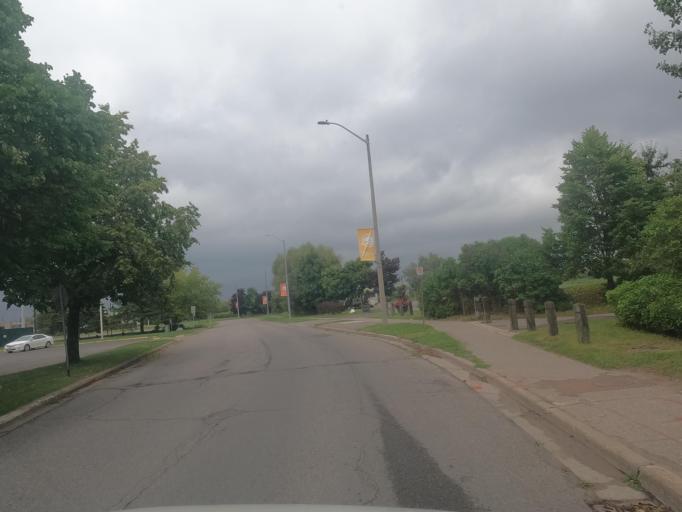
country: CA
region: Ontario
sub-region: Algoma
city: Sault Ste. Marie
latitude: 46.5152
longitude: -84.3469
